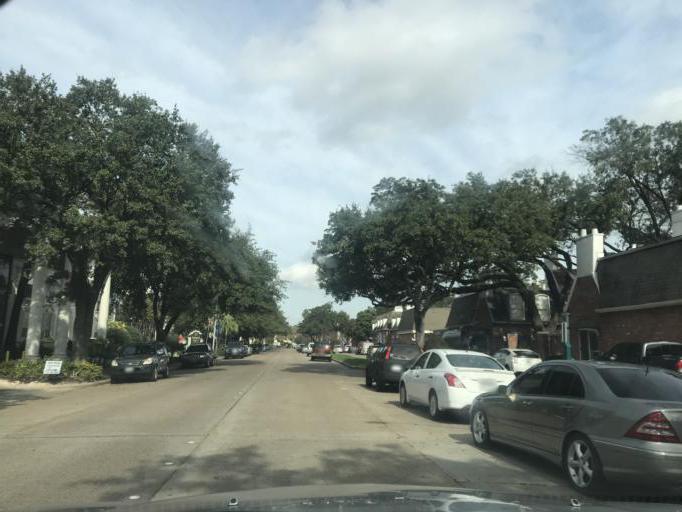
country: US
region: Texas
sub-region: Harris County
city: Piney Point Village
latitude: 29.7383
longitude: -95.4983
